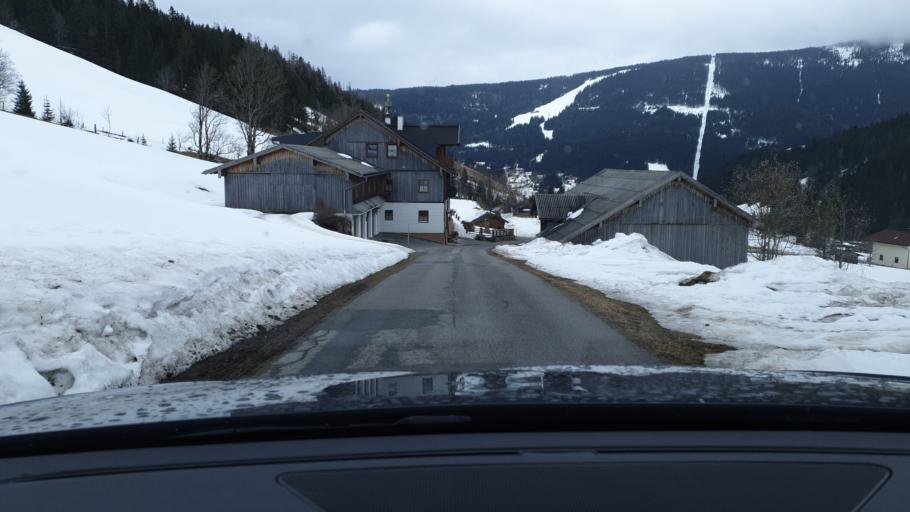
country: AT
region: Salzburg
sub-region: Politischer Bezirk Sankt Johann im Pongau
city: Filzmoos
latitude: 47.4482
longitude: 13.5222
